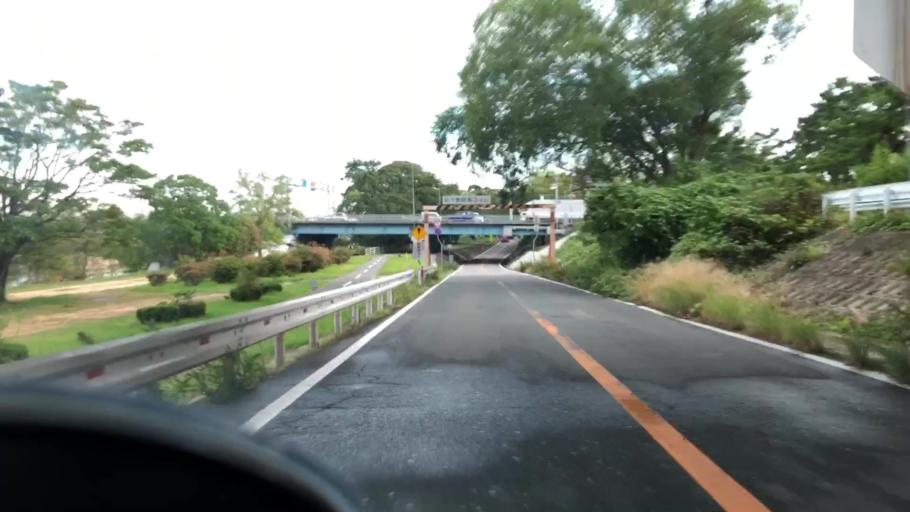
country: JP
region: Hyogo
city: Itami
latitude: 34.7659
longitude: 135.3724
